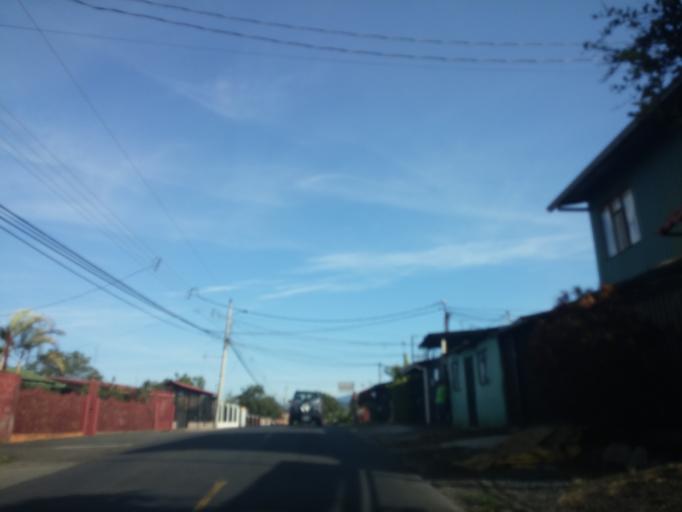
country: CR
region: Heredia
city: Mercedes
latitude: 10.0077
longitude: -84.1448
